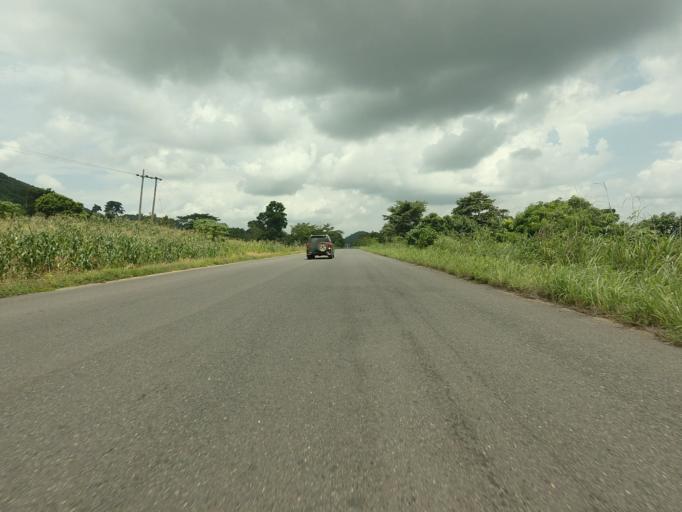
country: GH
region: Volta
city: Ho
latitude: 6.4432
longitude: 0.1738
